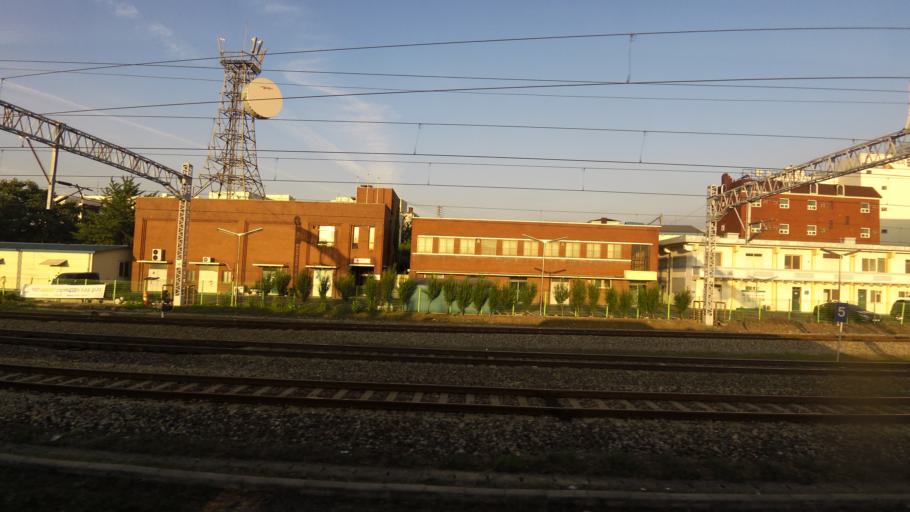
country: KR
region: Chungcheongnam-do
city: Cheonan
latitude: 36.8104
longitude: 127.1461
